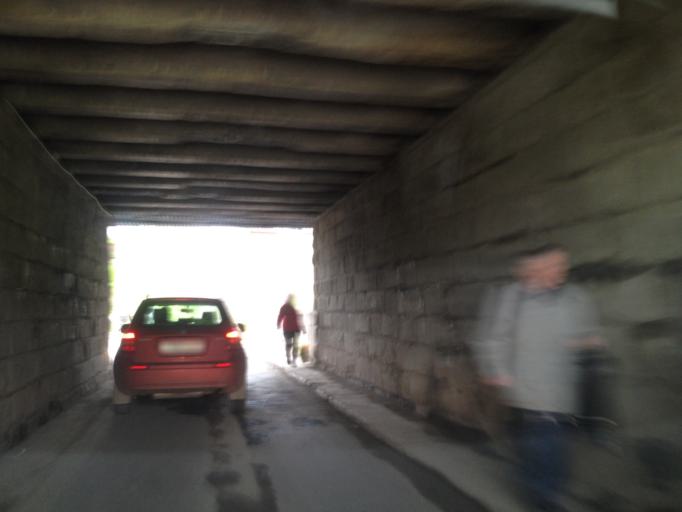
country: RU
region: Sverdlovsk
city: Yekaterinburg
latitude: 56.8588
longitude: 60.5803
